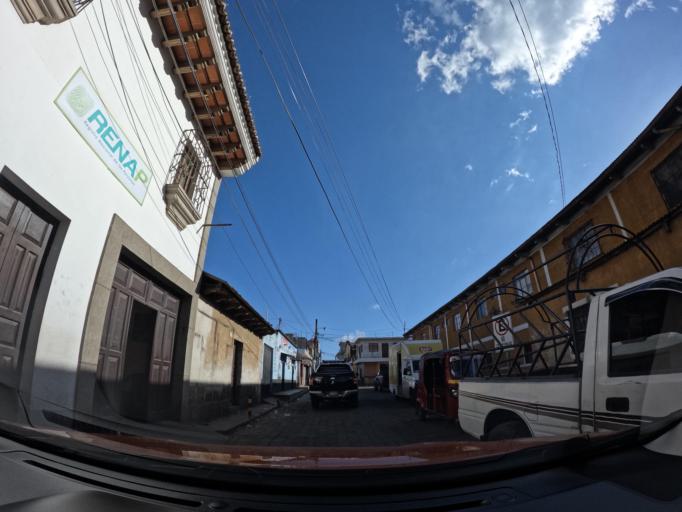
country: GT
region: Sacatepequez
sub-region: Municipio de Santa Maria de Jesus
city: Santa Maria de Jesus
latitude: 14.4938
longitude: -90.7087
